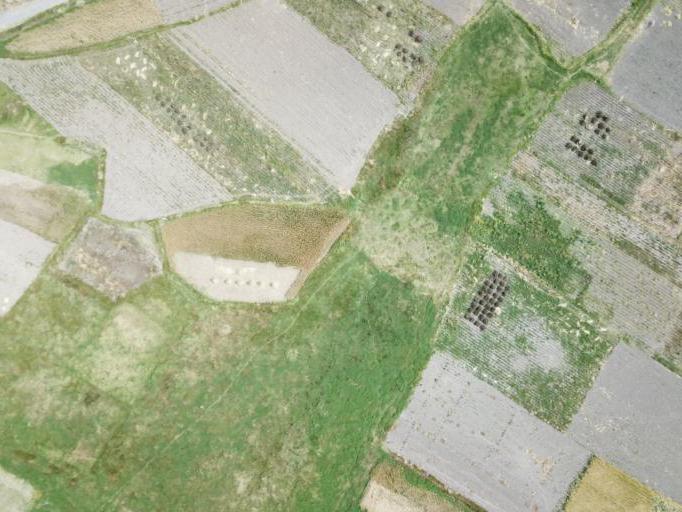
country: BO
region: La Paz
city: Achacachi
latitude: -16.0523
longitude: -68.8194
